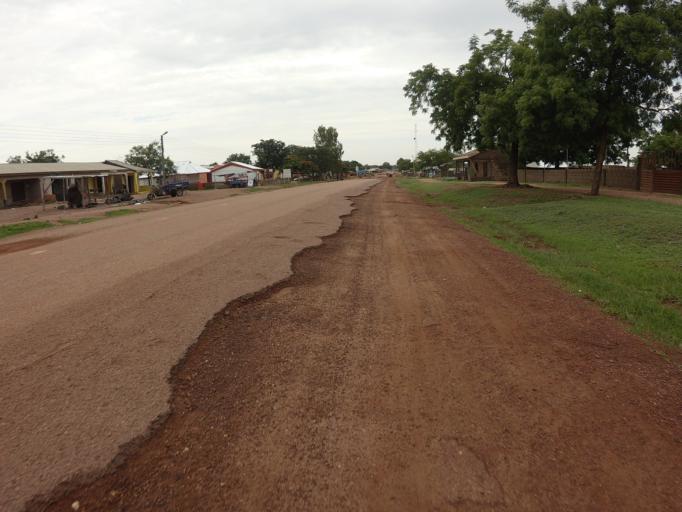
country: GH
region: Upper East
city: Bawku
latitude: 10.9358
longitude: -0.4962
